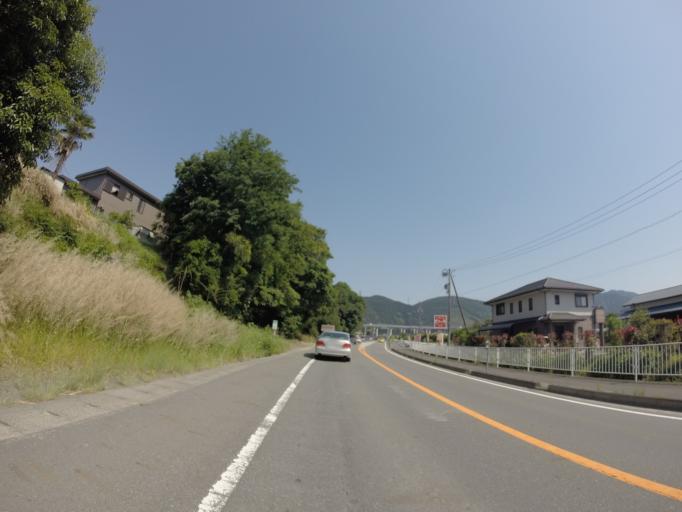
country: JP
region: Shizuoka
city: Fujinomiya
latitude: 35.1865
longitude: 138.6007
